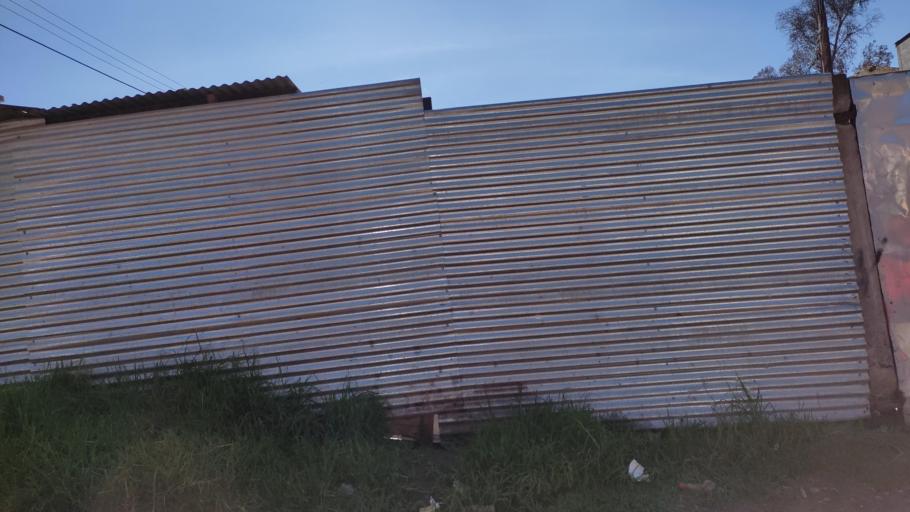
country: GT
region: Quetzaltenango
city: Quetzaltenango
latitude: 14.8551
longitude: -91.5244
